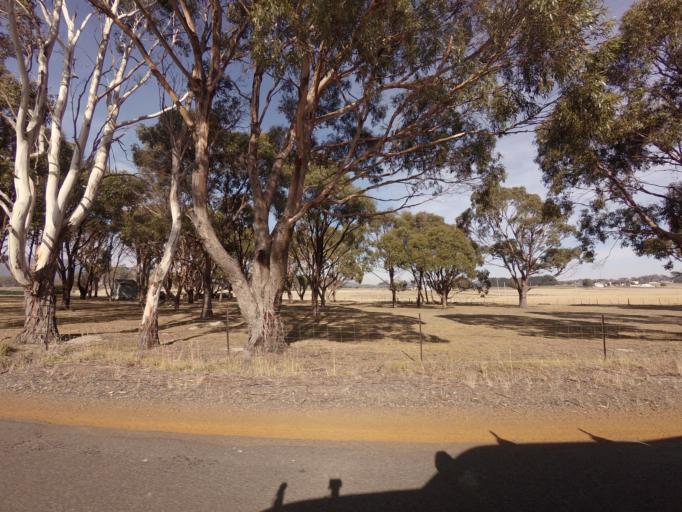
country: AU
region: Tasmania
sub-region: Sorell
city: Sorell
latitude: -42.4467
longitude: 147.4646
